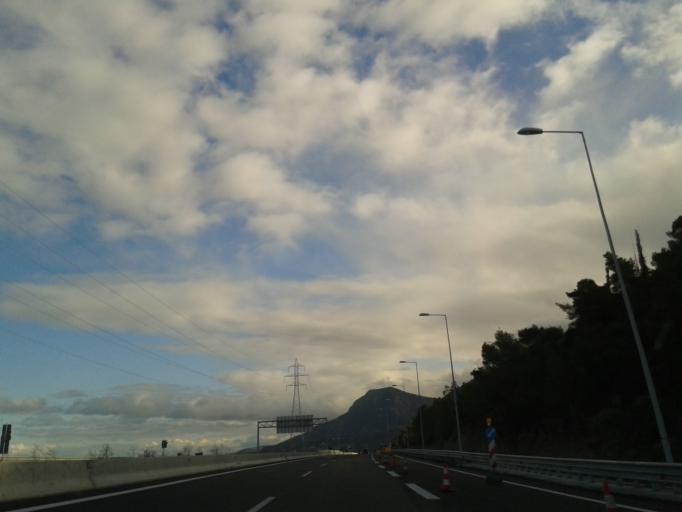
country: GR
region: Peloponnese
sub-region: Nomos Korinthias
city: Xylokastro
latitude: 38.1283
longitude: 22.5004
